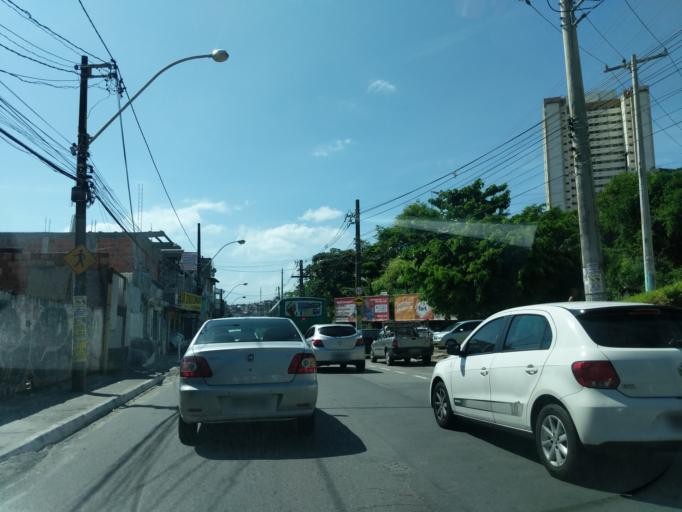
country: BR
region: Bahia
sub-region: Salvador
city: Salvador
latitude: -12.9554
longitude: -38.4429
